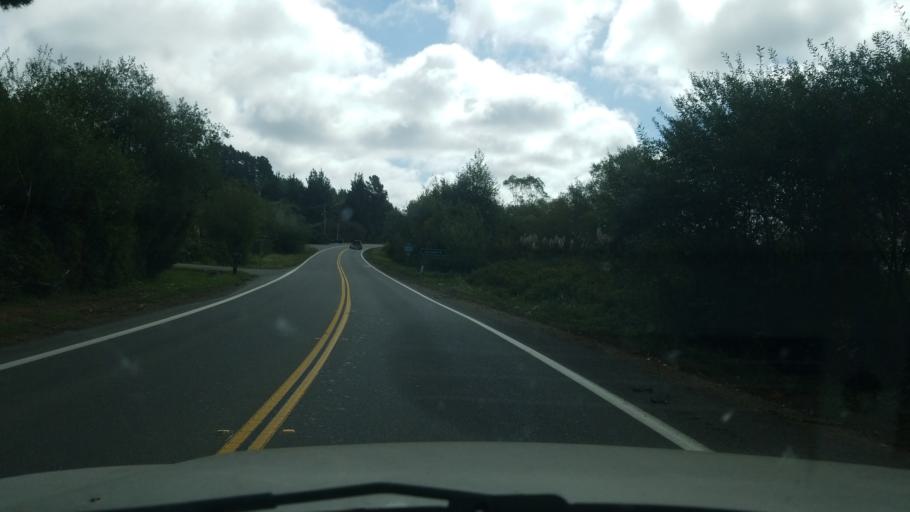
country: US
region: California
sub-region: Humboldt County
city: Fortuna
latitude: 40.6197
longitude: -124.2088
